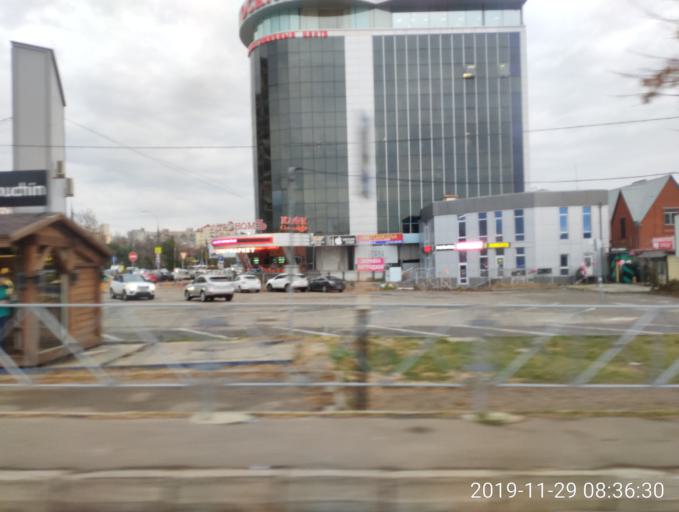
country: RU
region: Krasnodarskiy
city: Krasnodar
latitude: 45.0547
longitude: 39.0027
